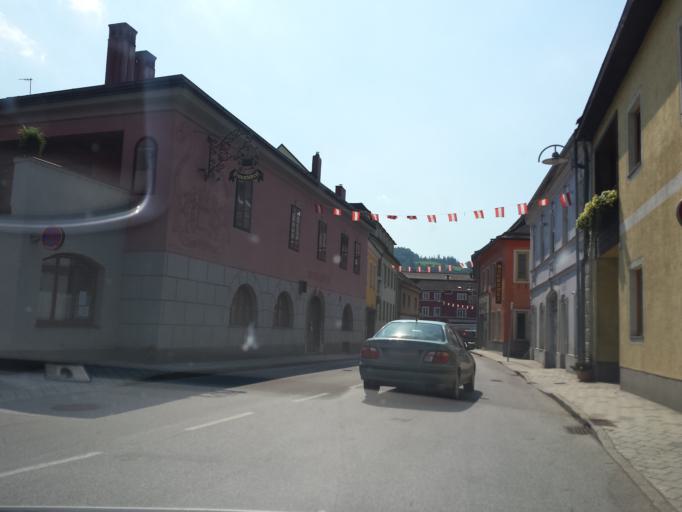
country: AT
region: Lower Austria
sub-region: Politischer Bezirk Lilienfeld
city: Hainfeld
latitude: 48.0342
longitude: 15.7754
